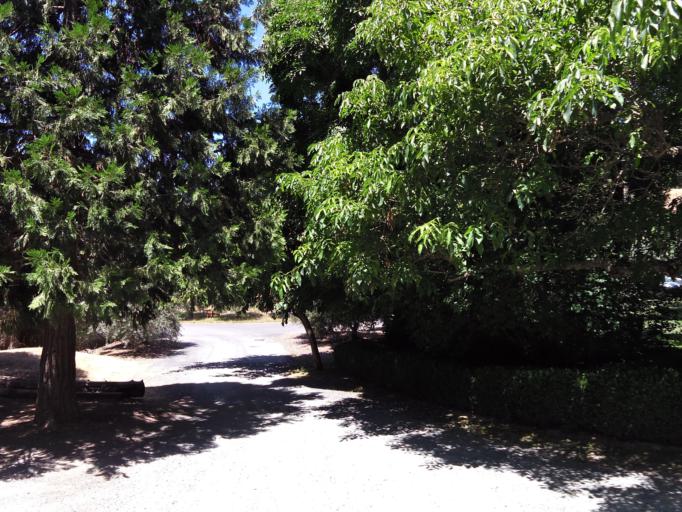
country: US
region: California
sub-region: Napa County
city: Deer Park
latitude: 38.5482
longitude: -122.4901
